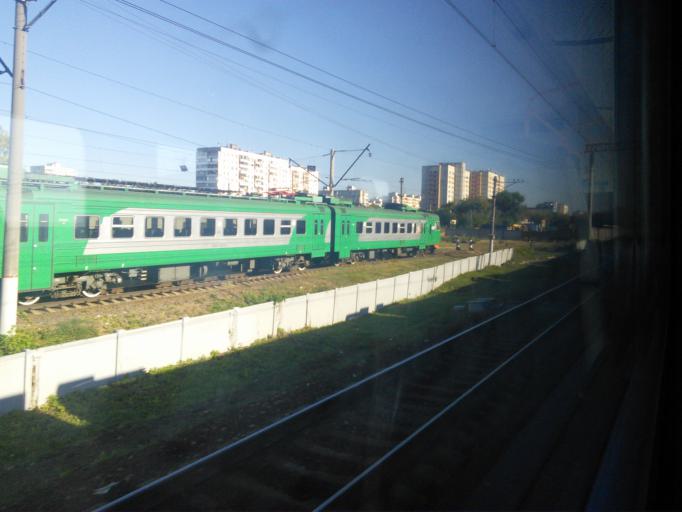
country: RU
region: Moscow
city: Mar'ino
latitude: 55.6684
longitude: 37.7247
